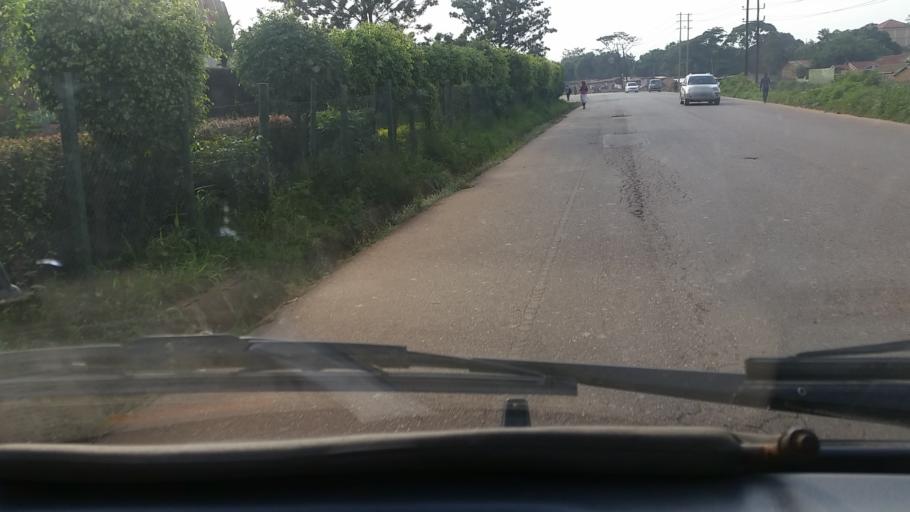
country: UG
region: Central Region
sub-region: Wakiso District
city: Kireka
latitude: 0.3456
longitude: 32.6574
